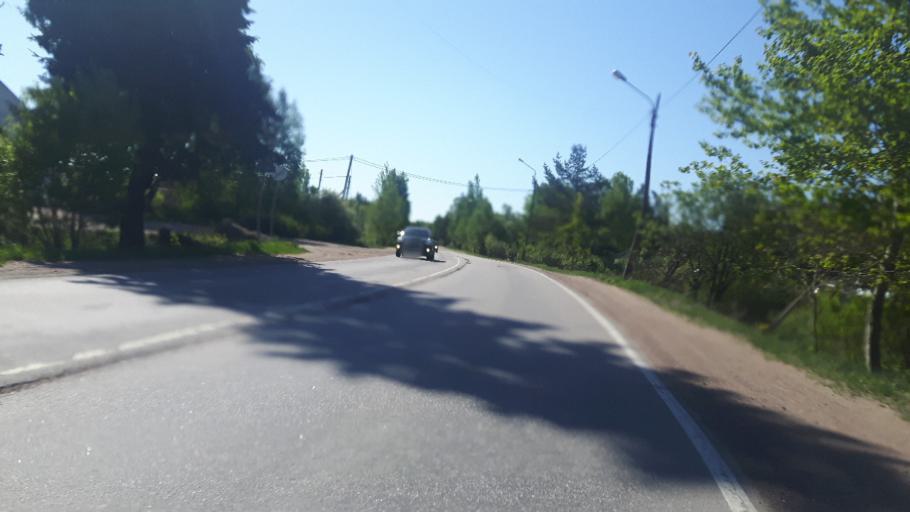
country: RU
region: Leningrad
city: Vyborg
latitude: 60.6523
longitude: 28.7446
